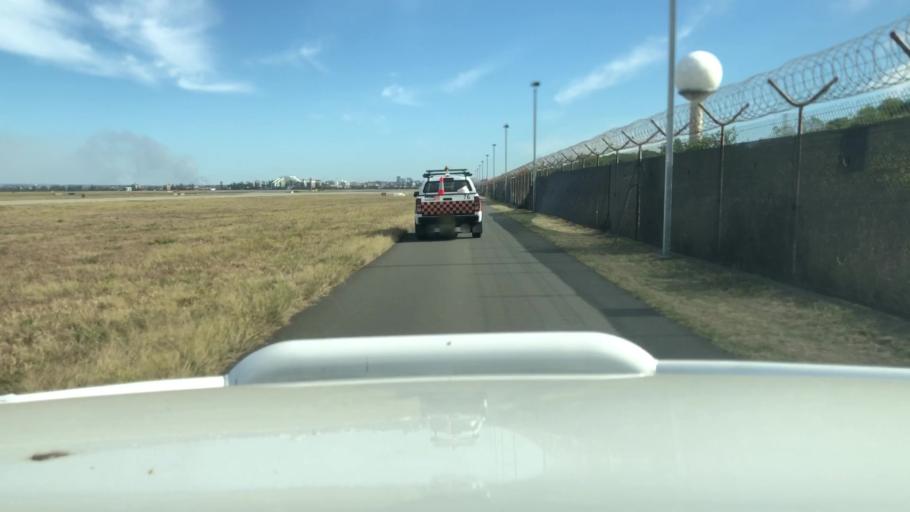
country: AU
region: New South Wales
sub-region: Botany Bay
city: Botany
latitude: -33.9500
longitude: 151.1838
